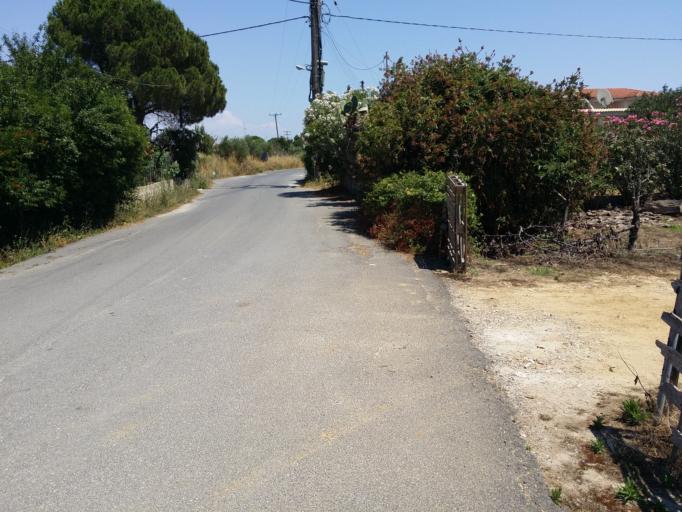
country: GR
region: Ionian Islands
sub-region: Nomos Kerkyras
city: Perivoli
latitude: 39.4292
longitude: 19.9448
